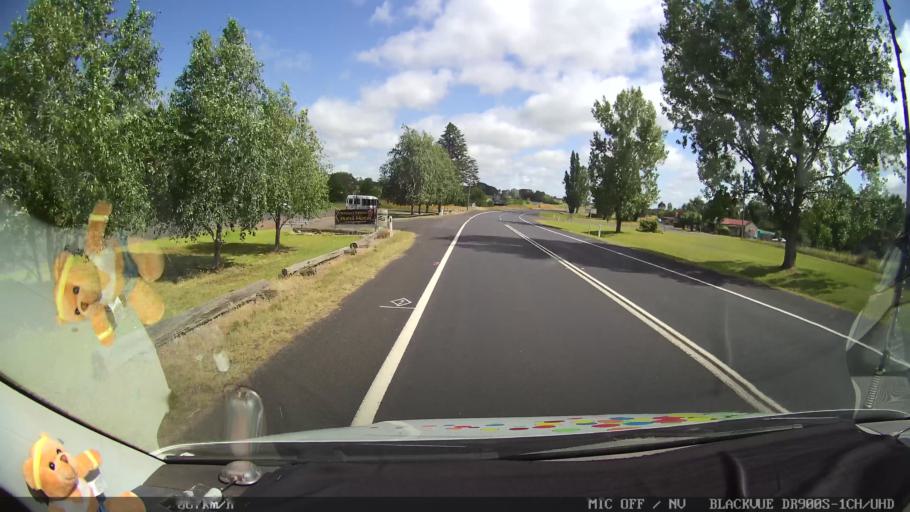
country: AU
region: New South Wales
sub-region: Glen Innes Severn
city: Glen Innes
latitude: -29.9268
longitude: 151.7241
